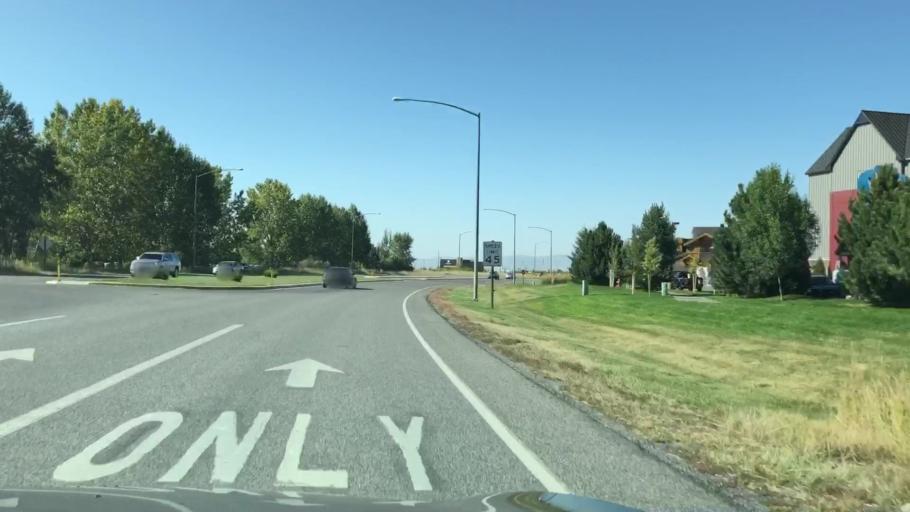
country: US
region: Montana
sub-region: Gallatin County
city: Bozeman
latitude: 45.7125
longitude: -111.0669
